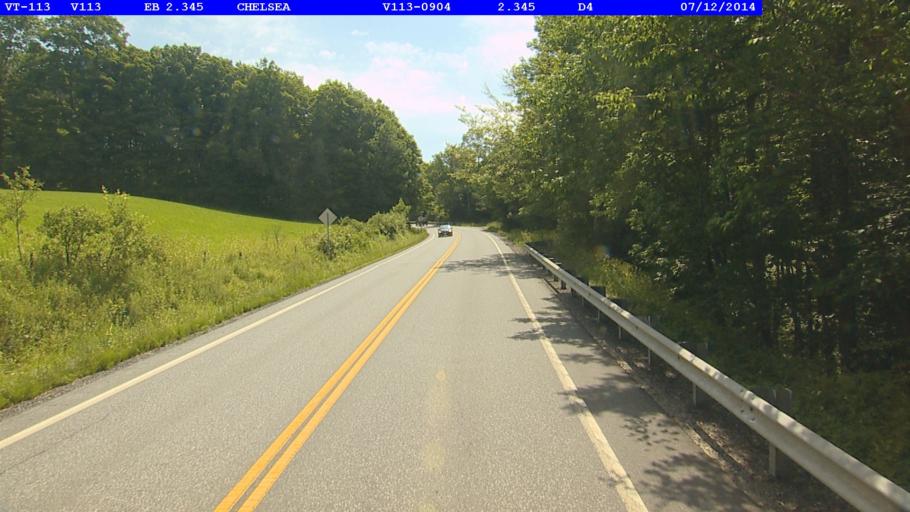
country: US
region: Vermont
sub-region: Orange County
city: Chelsea
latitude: 43.9911
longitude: -72.4058
